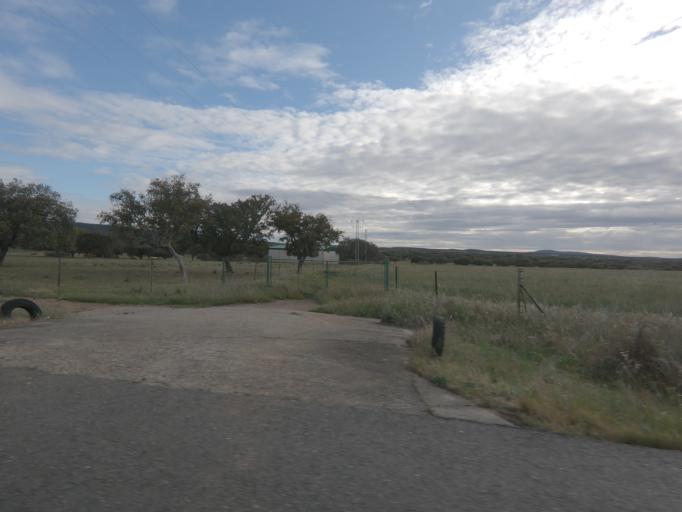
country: ES
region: Extremadura
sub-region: Provincia de Caceres
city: Torrejoncillo
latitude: 39.8656
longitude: -6.4348
